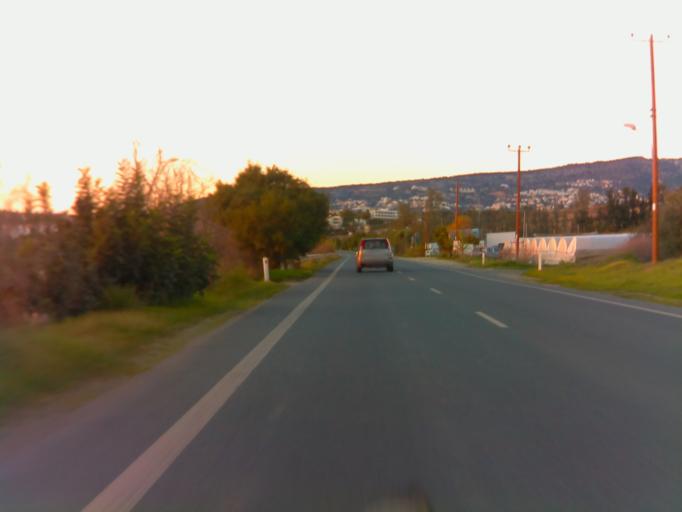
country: CY
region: Pafos
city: Kissonerga
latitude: 34.8458
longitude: 32.3864
